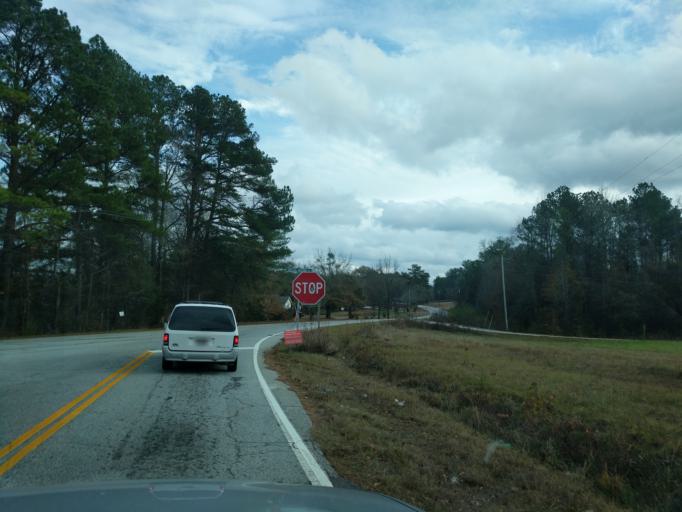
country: US
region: South Carolina
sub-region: Greenwood County
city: Ware Shoals
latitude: 34.4055
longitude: -82.2058
